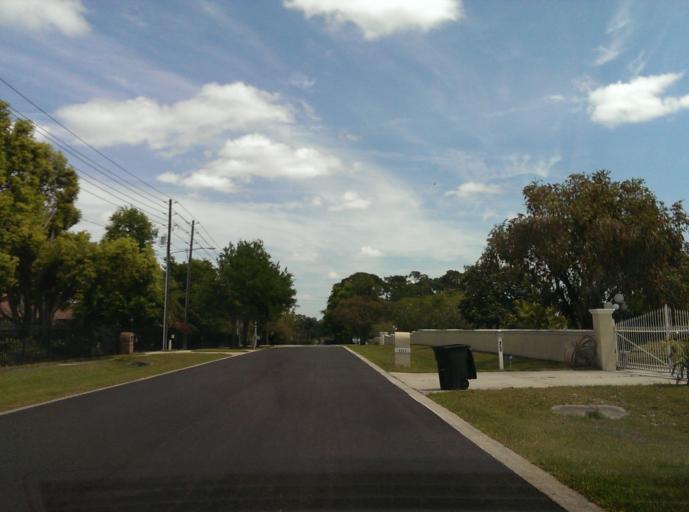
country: US
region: Florida
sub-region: Orange County
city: Bay Hill
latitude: 28.4773
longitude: -81.5013
